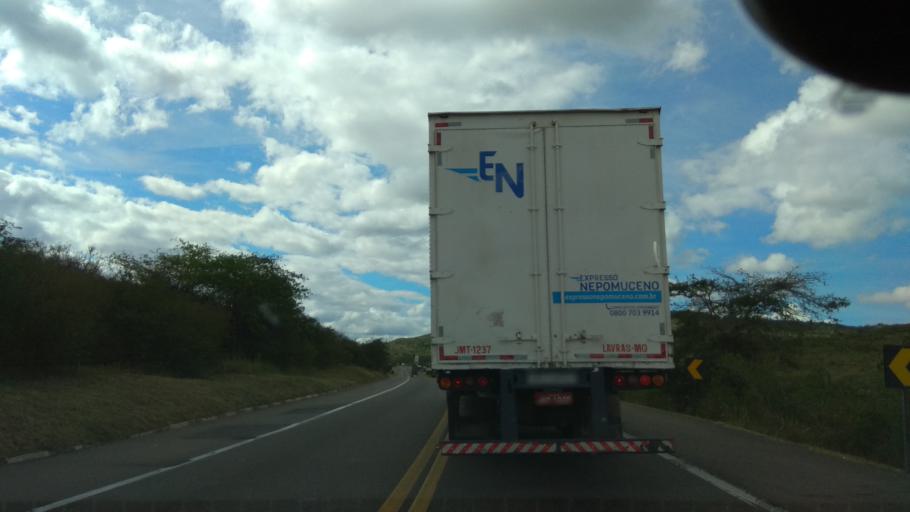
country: BR
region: Bahia
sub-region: Amargosa
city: Amargosa
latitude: -12.9116
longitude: -39.8655
